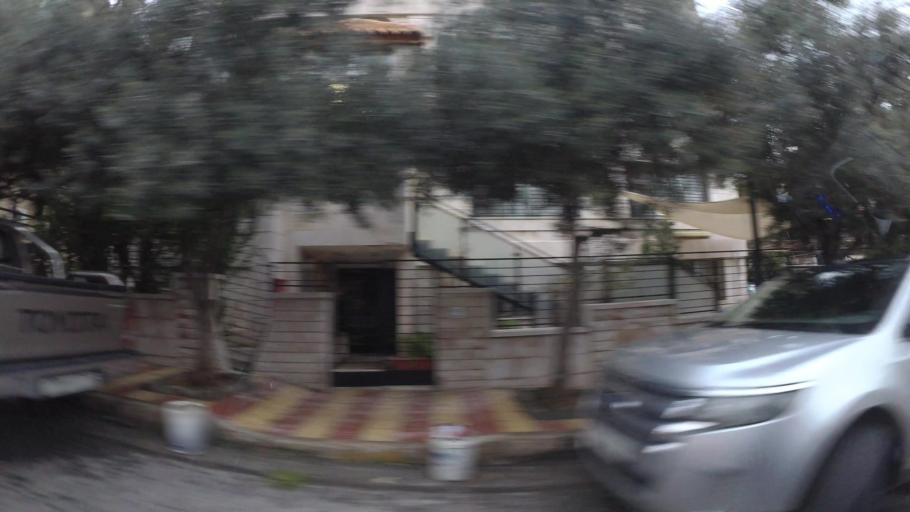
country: JO
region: Amman
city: Amman
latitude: 31.9665
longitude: 35.8848
